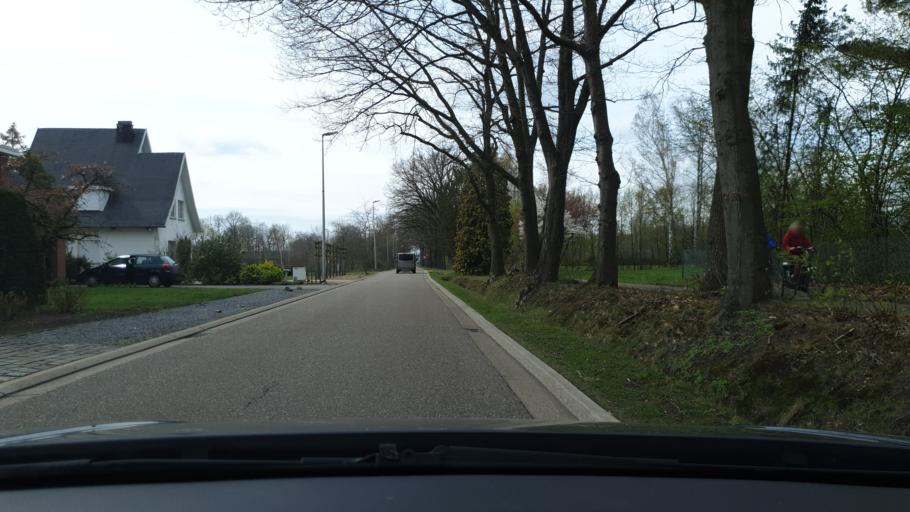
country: BE
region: Flanders
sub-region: Provincie Limburg
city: Zonhoven
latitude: 50.9606
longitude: 5.3700
